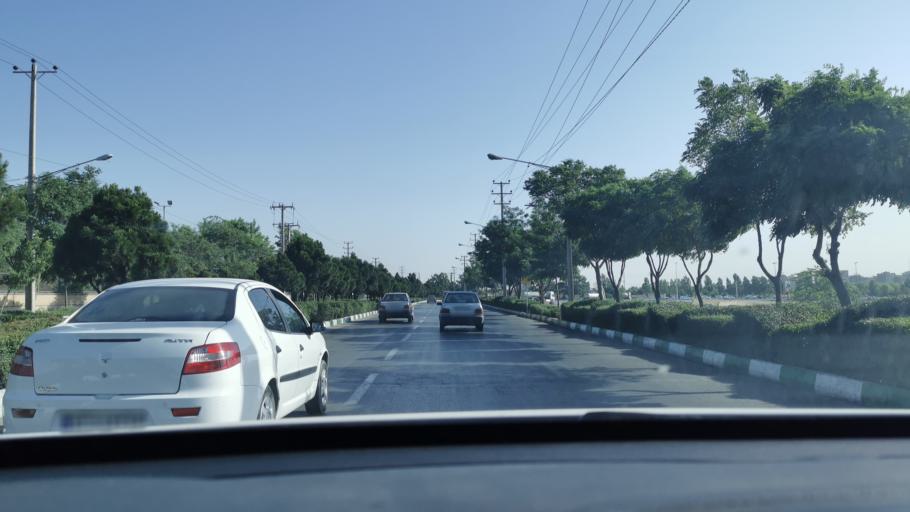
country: IR
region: Razavi Khorasan
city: Mashhad
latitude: 36.3428
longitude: 59.5080
